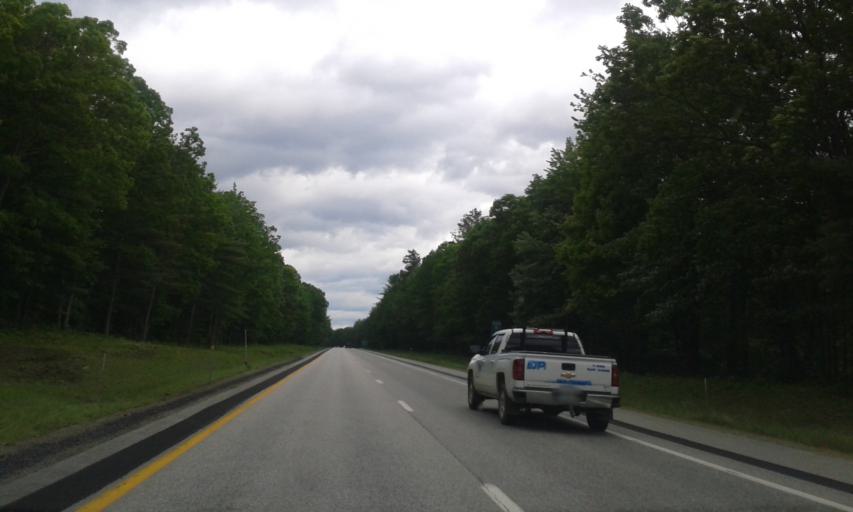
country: US
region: New Hampshire
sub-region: Merrimack County
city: Canterbury
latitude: 43.3131
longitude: -71.5877
